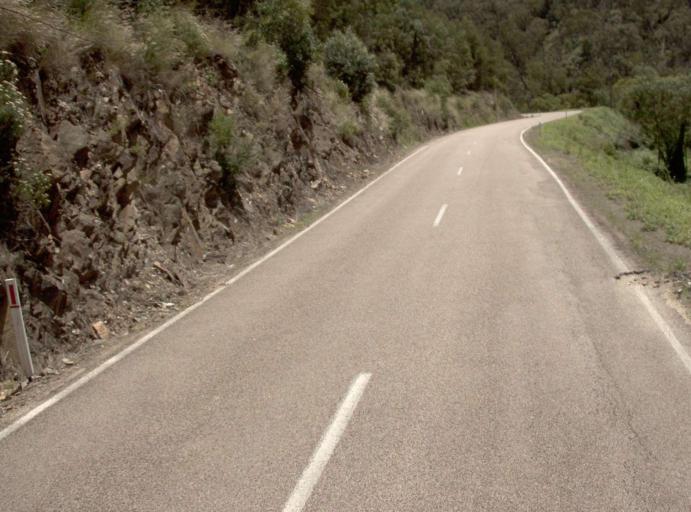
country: AU
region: Victoria
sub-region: East Gippsland
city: Lakes Entrance
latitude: -37.5316
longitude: 147.8535
